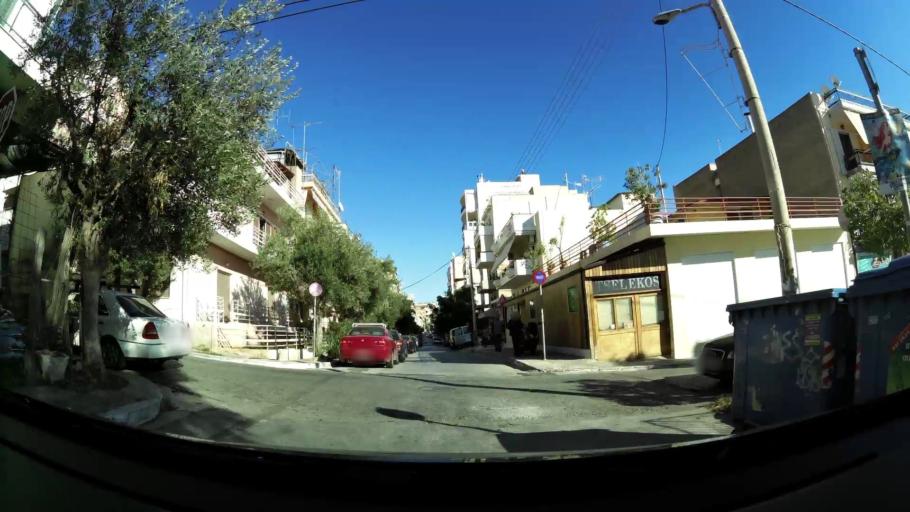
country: GR
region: Attica
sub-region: Nomos Piraios
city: Perama
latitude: 37.9665
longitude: 23.5658
